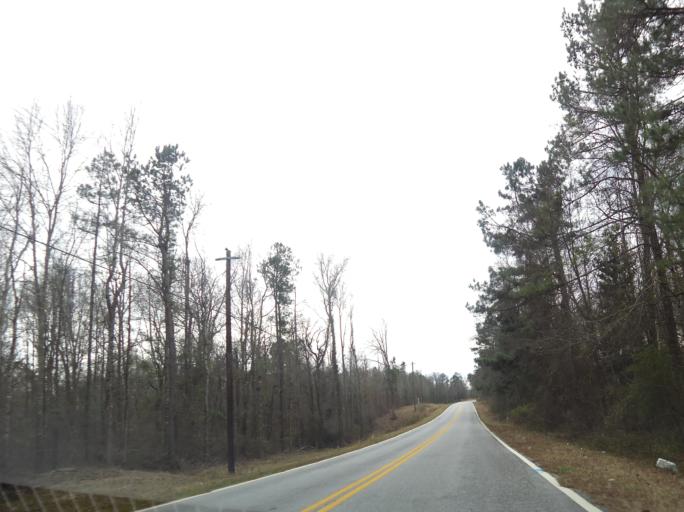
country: US
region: Georgia
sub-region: Bibb County
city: West Point
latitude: 32.8264
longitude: -83.7336
